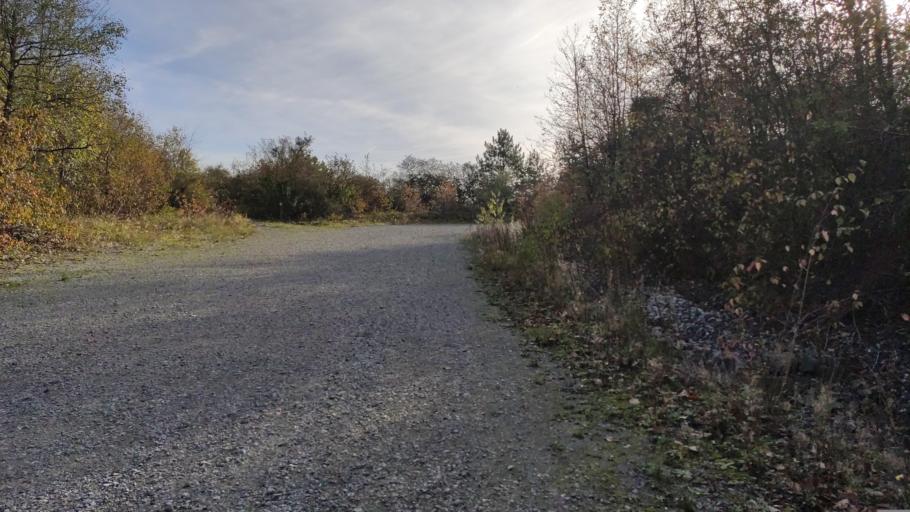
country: DE
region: North Rhine-Westphalia
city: Herten
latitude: 51.5657
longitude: 7.1637
